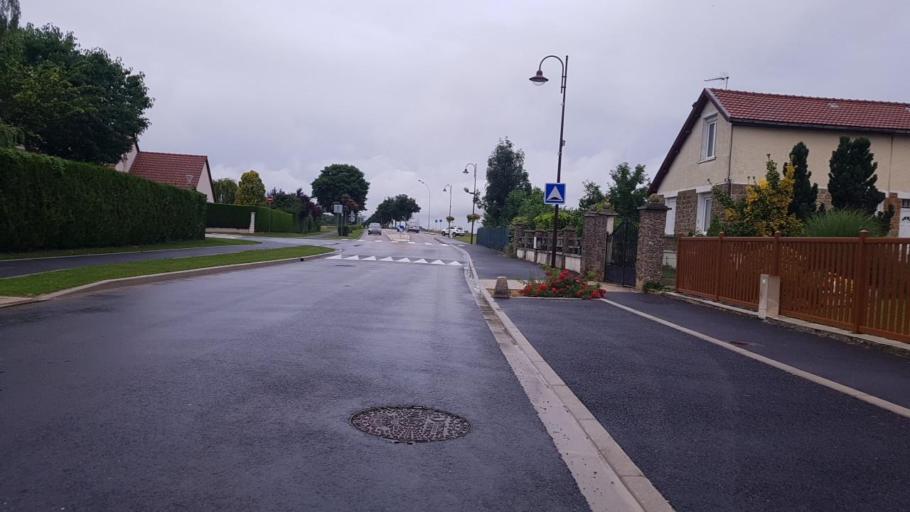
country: FR
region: Champagne-Ardenne
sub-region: Departement de la Marne
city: Sarry
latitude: 48.9223
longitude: 4.4005
